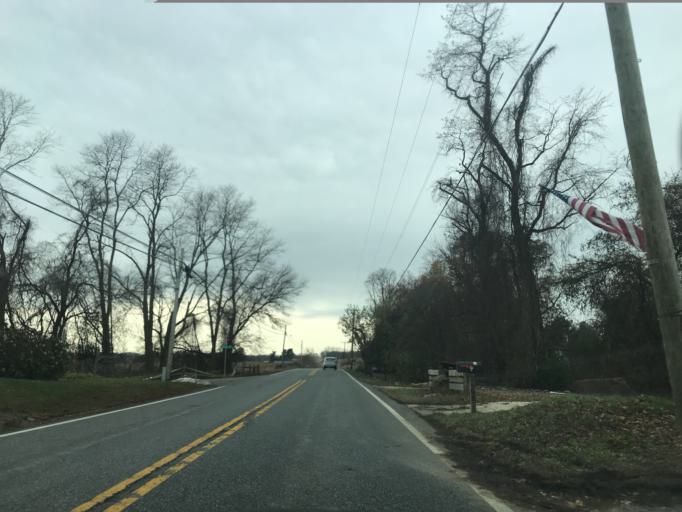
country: US
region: Maryland
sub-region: Harford County
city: Bel Air North
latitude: 39.6005
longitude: -76.3410
